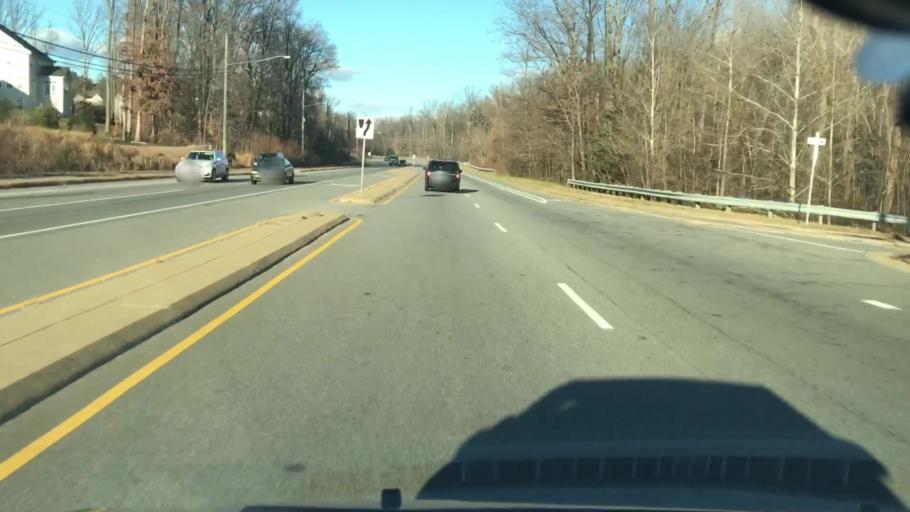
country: US
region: Virginia
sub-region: Fairfax County
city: Newington
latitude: 38.7334
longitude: -77.1708
